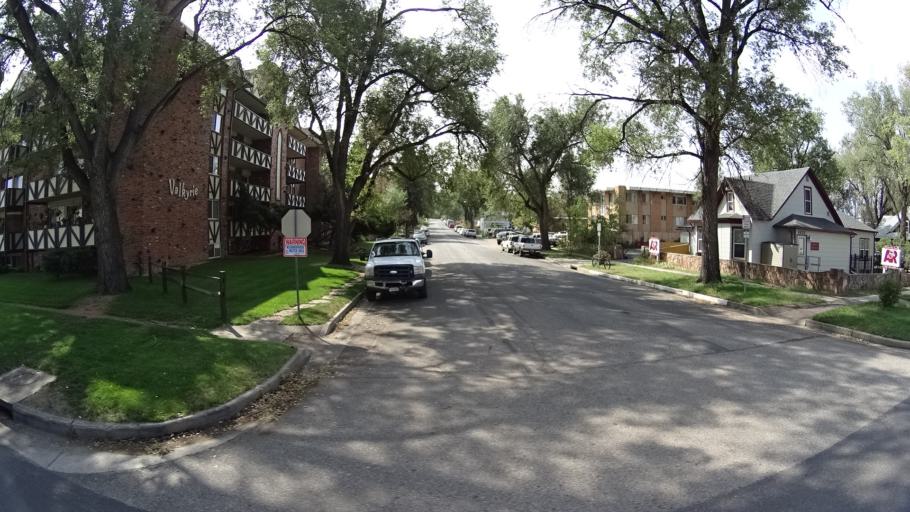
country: US
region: Colorado
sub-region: El Paso County
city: Colorado Springs
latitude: 38.8357
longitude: -104.7931
